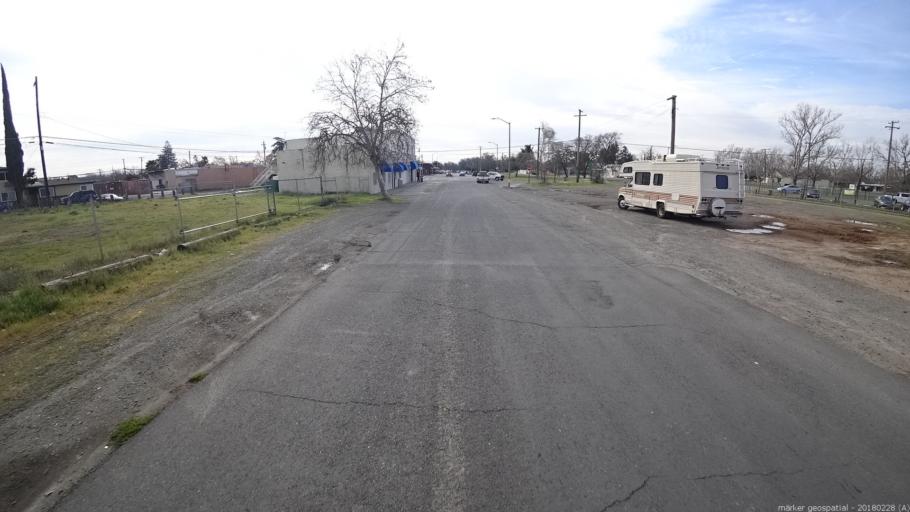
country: US
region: California
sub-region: Sacramento County
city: Rio Linda
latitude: 38.6918
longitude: -121.4495
